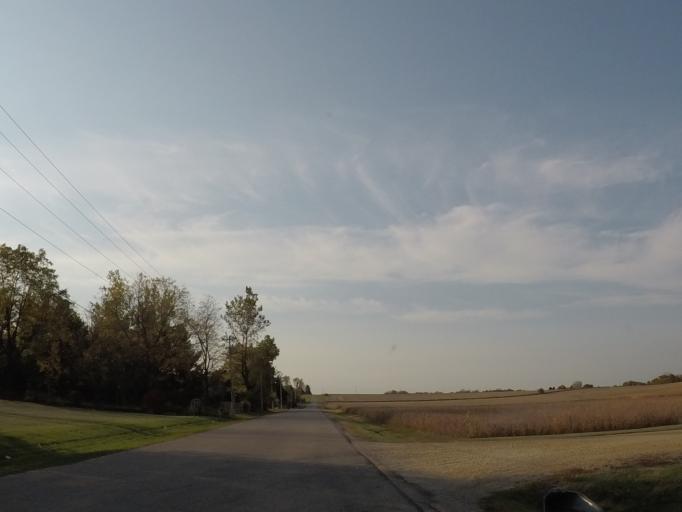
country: US
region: Wisconsin
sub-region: Dane County
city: Cross Plains
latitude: 43.0586
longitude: -89.6010
